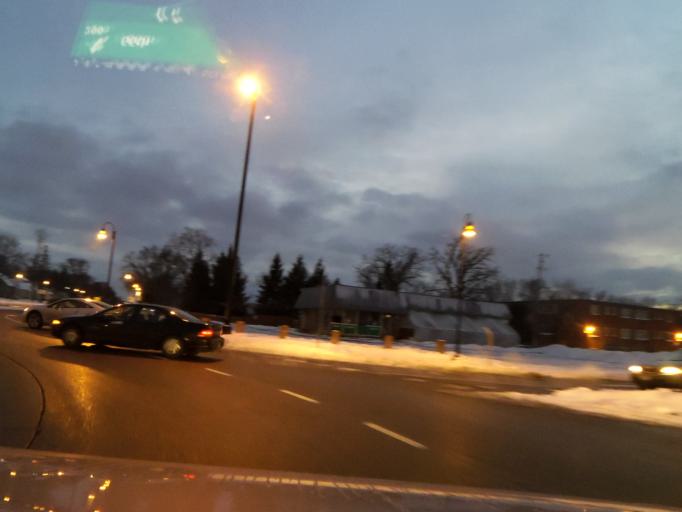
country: US
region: Minnesota
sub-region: Hennepin County
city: Richfield
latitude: 44.8836
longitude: -93.2680
